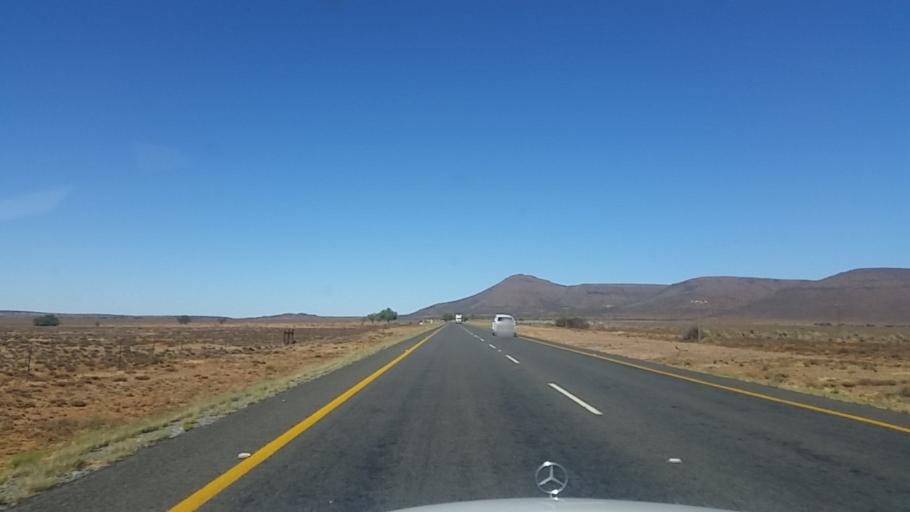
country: ZA
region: Eastern Cape
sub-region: Cacadu District Municipality
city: Graaff-Reinet
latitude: -32.0184
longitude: 24.6418
